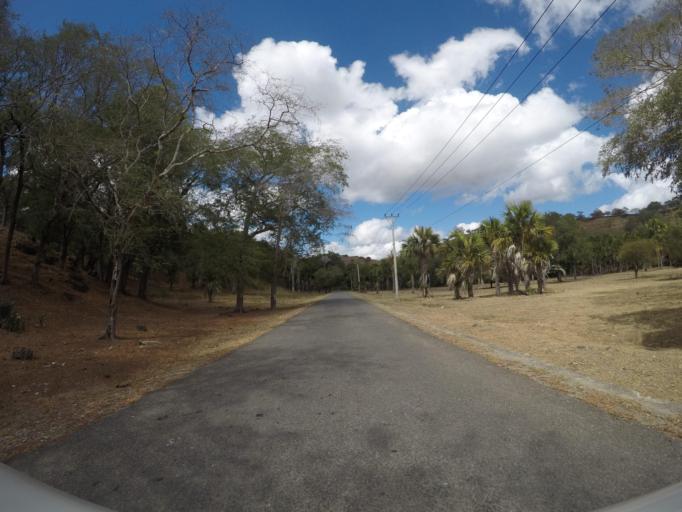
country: TL
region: Lautem
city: Lospalos
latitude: -8.4091
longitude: 126.8276
